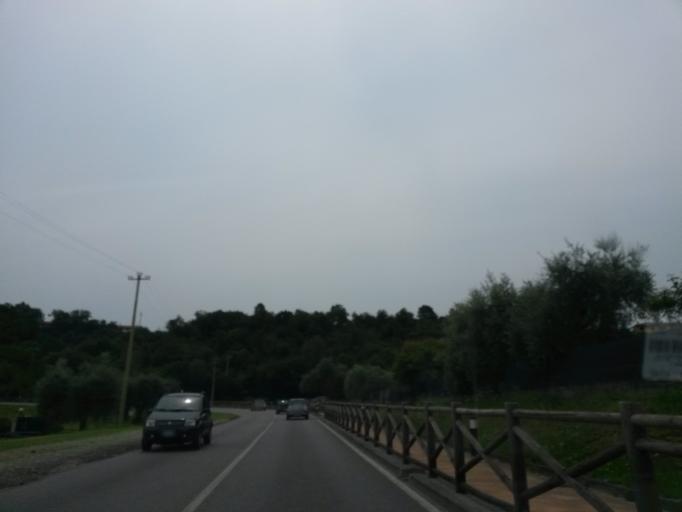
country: IT
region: Lombardy
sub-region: Provincia di Brescia
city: Cunettone-Villa
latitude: 45.5941
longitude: 10.5114
